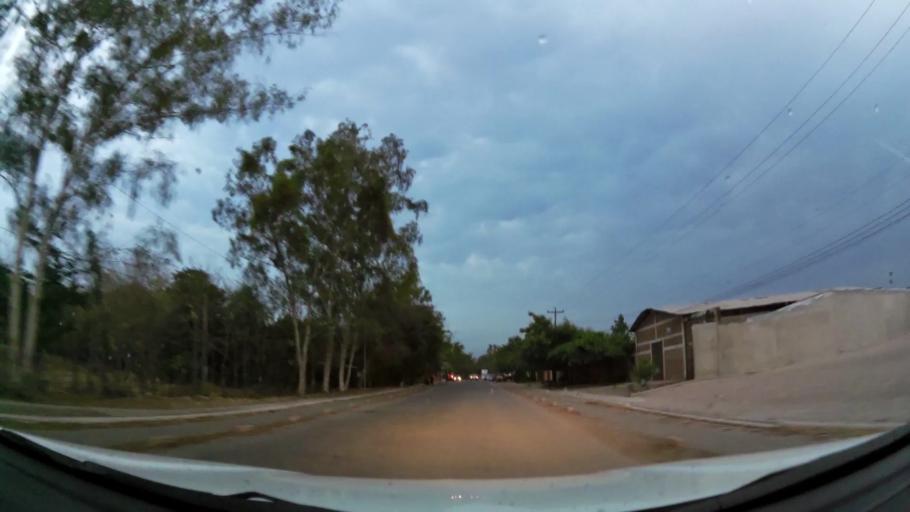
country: NI
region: Esteli
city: Esteli
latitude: 13.1064
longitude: -86.3592
